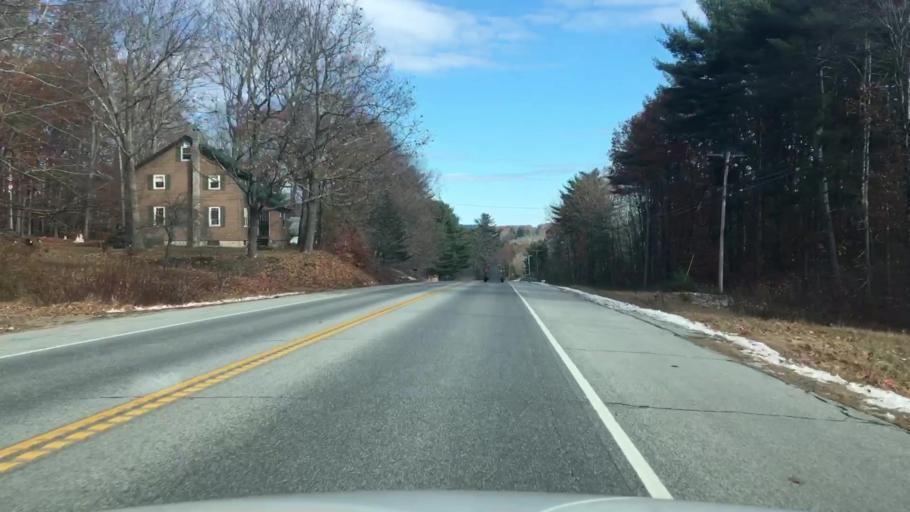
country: US
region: Maine
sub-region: Kennebec County
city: Winthrop
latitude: 44.3148
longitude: -69.9423
